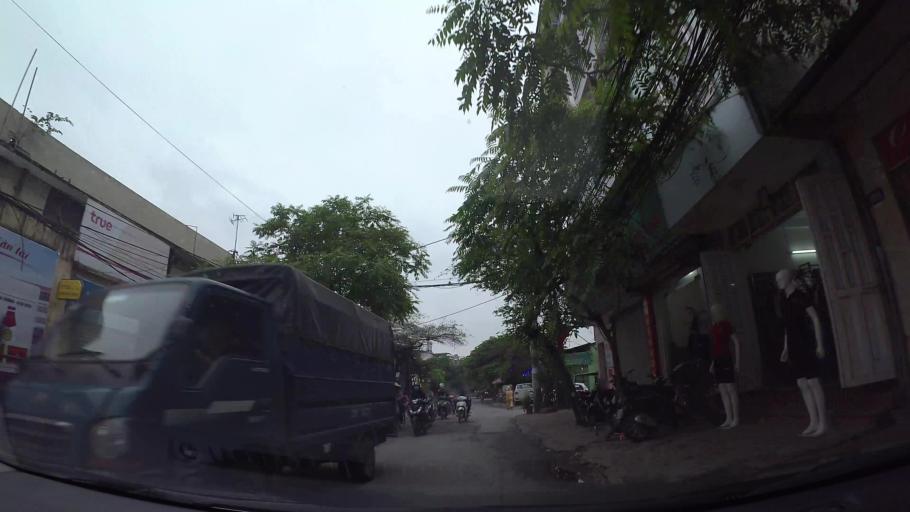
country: VN
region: Ha Noi
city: Hai BaTrung
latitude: 20.9973
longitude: 105.8797
